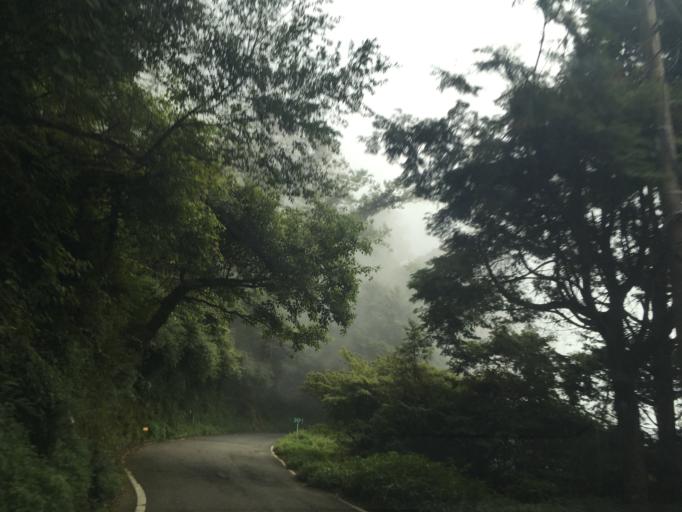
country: TW
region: Taiwan
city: Fengyuan
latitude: 24.2297
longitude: 120.9649
